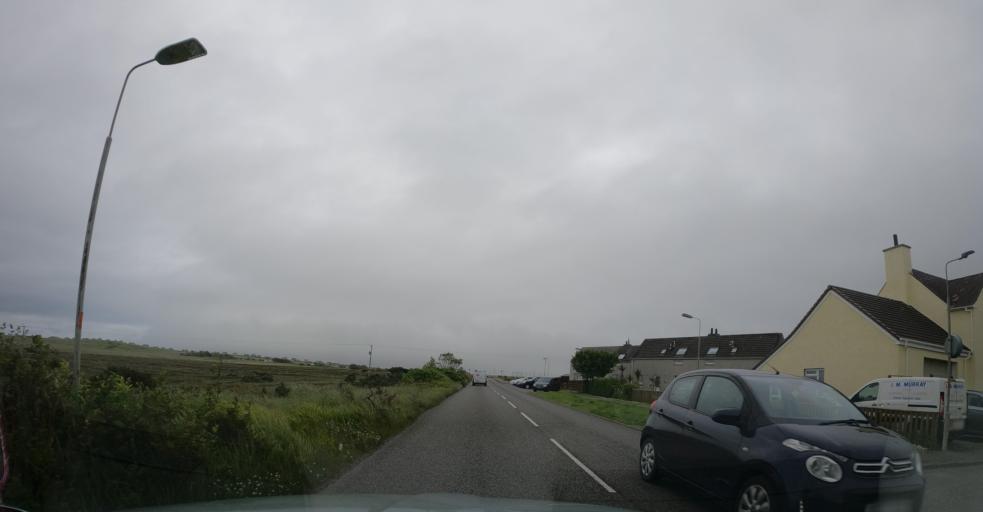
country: GB
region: Scotland
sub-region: Eilean Siar
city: Stornoway
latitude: 58.2087
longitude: -6.2597
